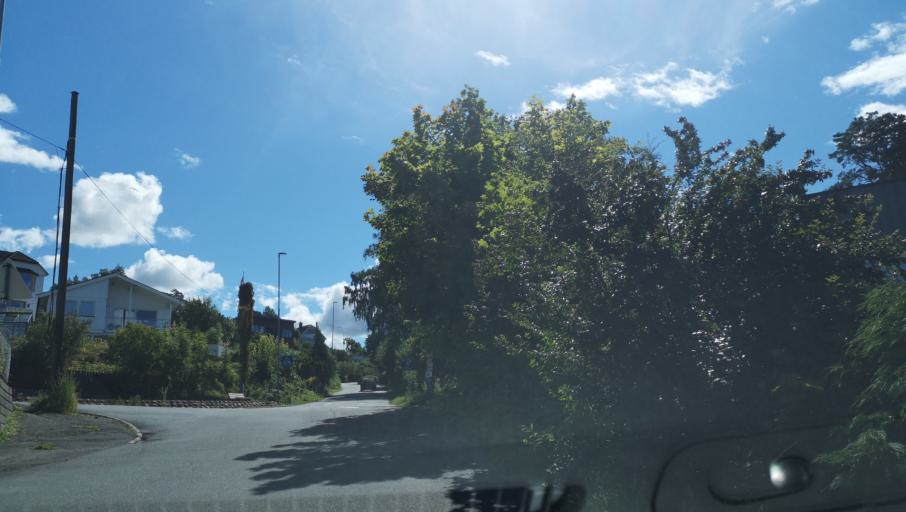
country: NO
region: Akershus
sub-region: Frogn
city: Drobak
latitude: 59.6532
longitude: 10.6392
